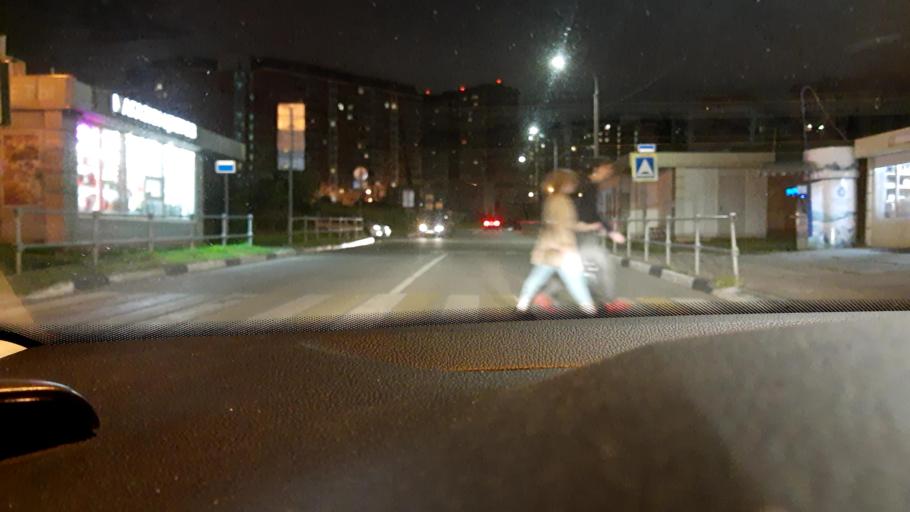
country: RU
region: Moskovskaya
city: Krasnogorsk
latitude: 55.8297
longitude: 37.2969
